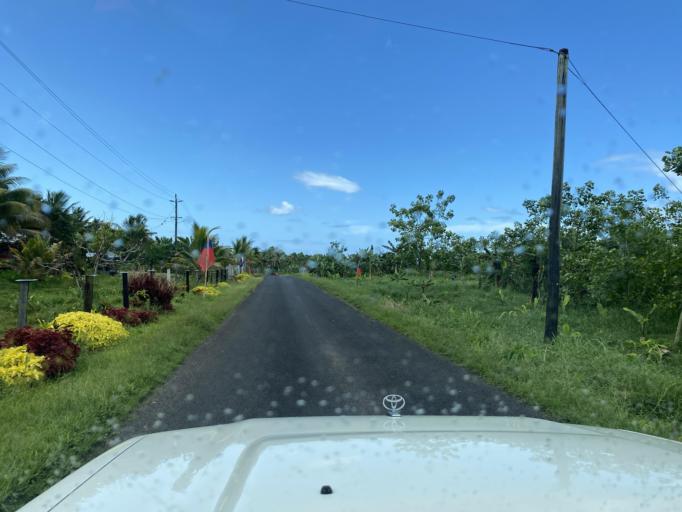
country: WS
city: Matavai
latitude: -13.9931
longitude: -171.5862
